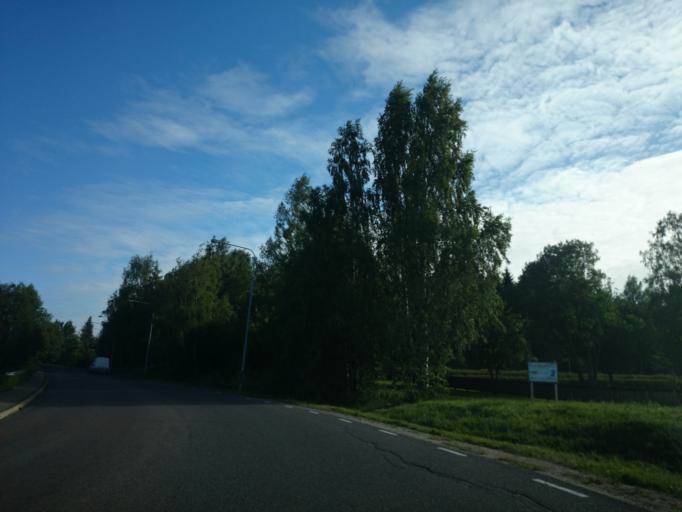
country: SE
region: Vaesternorrland
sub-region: Sundsvalls Kommun
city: Sundsvall
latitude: 62.4094
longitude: 17.3329
